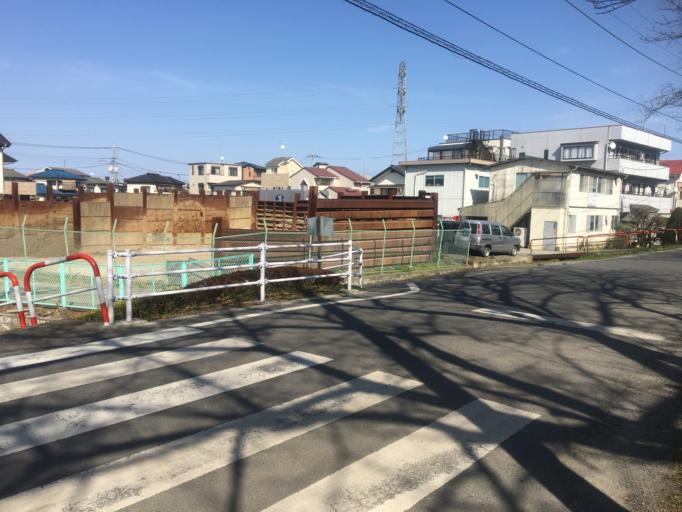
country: JP
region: Saitama
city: Shiki
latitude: 35.8309
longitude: 139.5969
